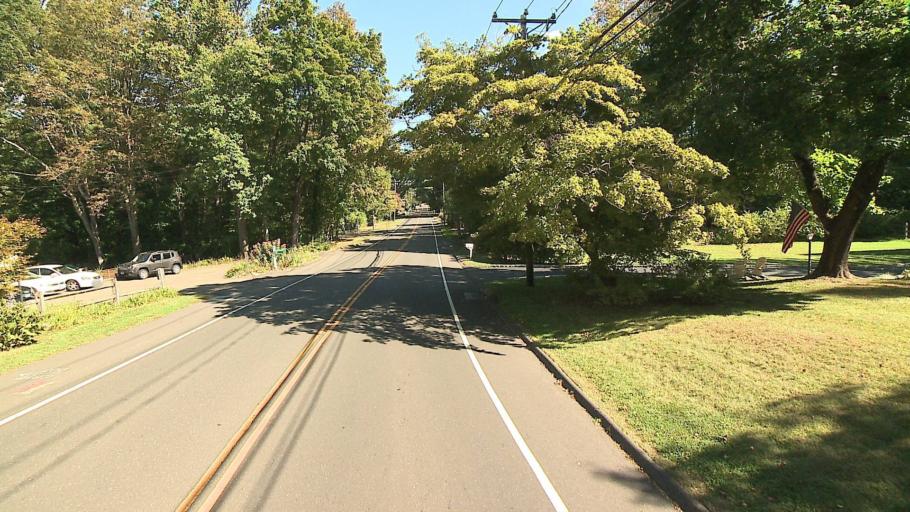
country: US
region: Connecticut
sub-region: Fairfield County
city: New Canaan
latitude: 41.1352
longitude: -73.4966
